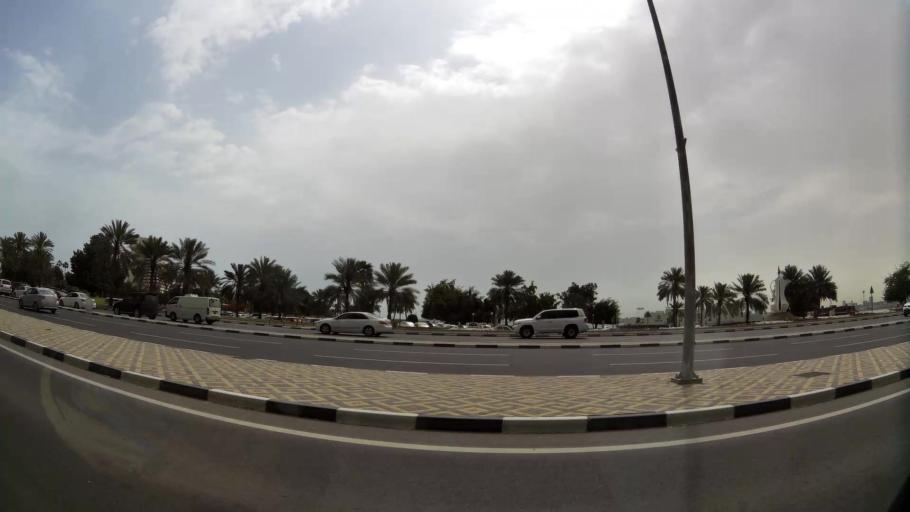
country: QA
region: Baladiyat ad Dawhah
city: Doha
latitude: 25.3184
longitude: 51.5305
